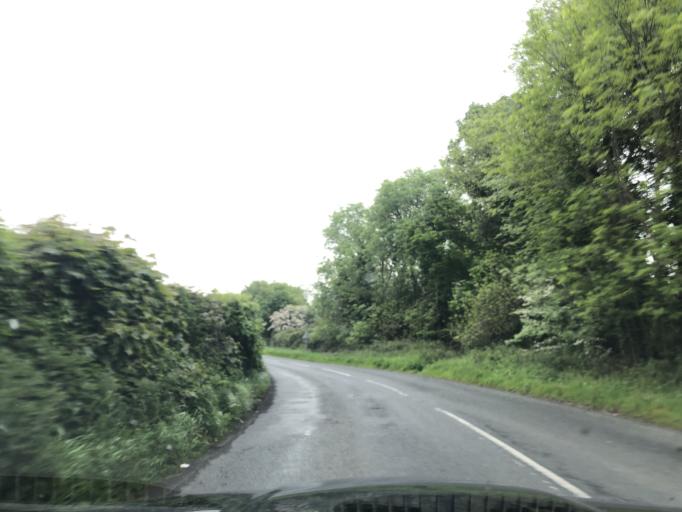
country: GB
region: Northern Ireland
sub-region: Down District
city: Castlewellan
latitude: 54.2258
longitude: -5.9427
